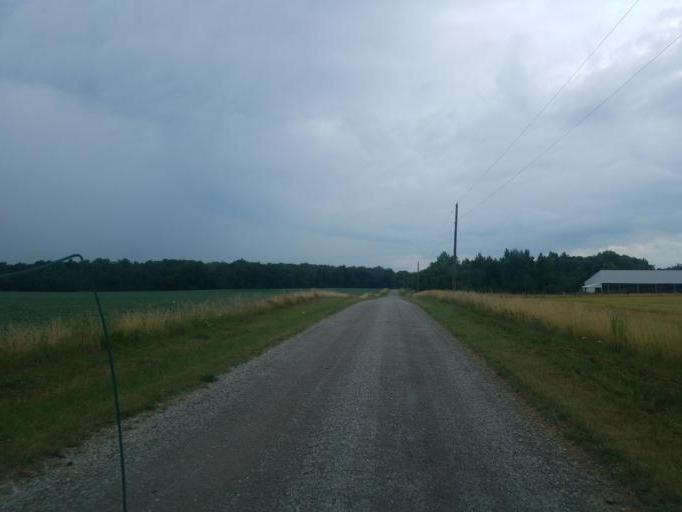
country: US
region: Ohio
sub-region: Defiance County
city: Hicksville
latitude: 41.3597
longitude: -84.8040
